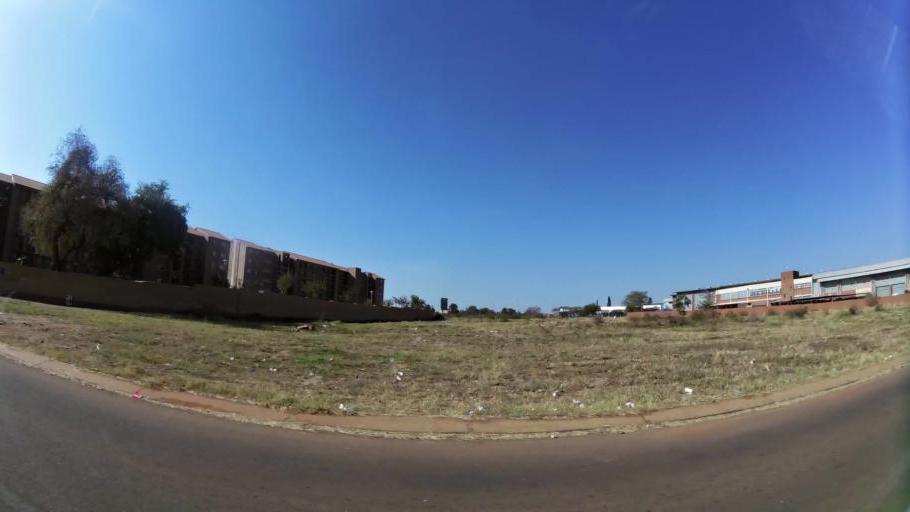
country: ZA
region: Gauteng
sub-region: City of Tshwane Metropolitan Municipality
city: Pretoria
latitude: -25.6775
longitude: 28.1909
